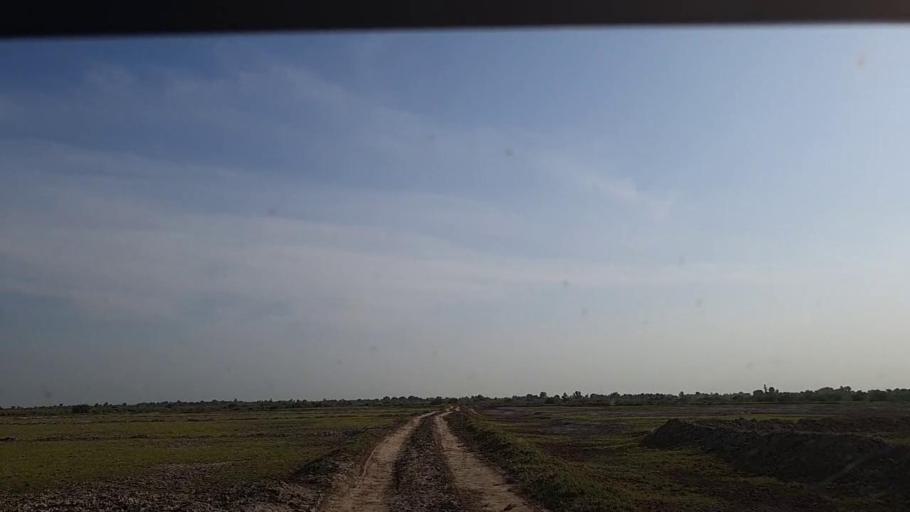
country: PK
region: Sindh
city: Adilpur
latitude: 27.9090
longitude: 69.2129
